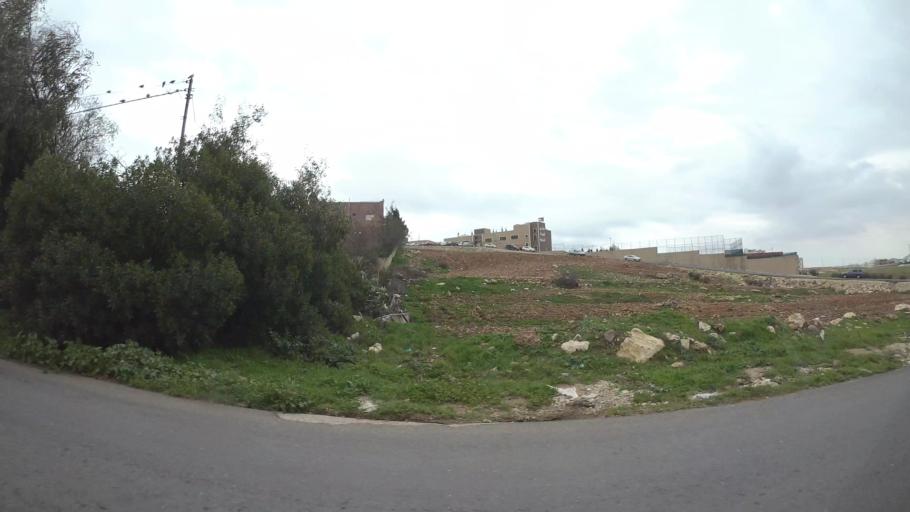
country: JO
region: Amman
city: Wadi as Sir
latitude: 31.9311
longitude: 35.8503
